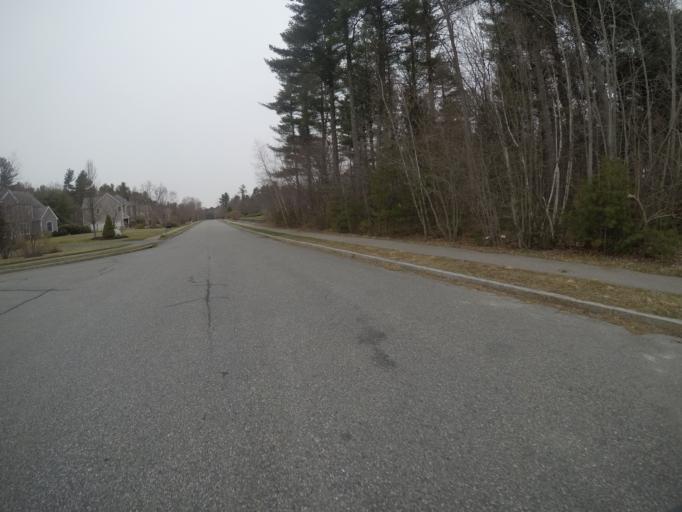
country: US
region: Massachusetts
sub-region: Bristol County
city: Easton
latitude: 42.0169
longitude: -71.1119
